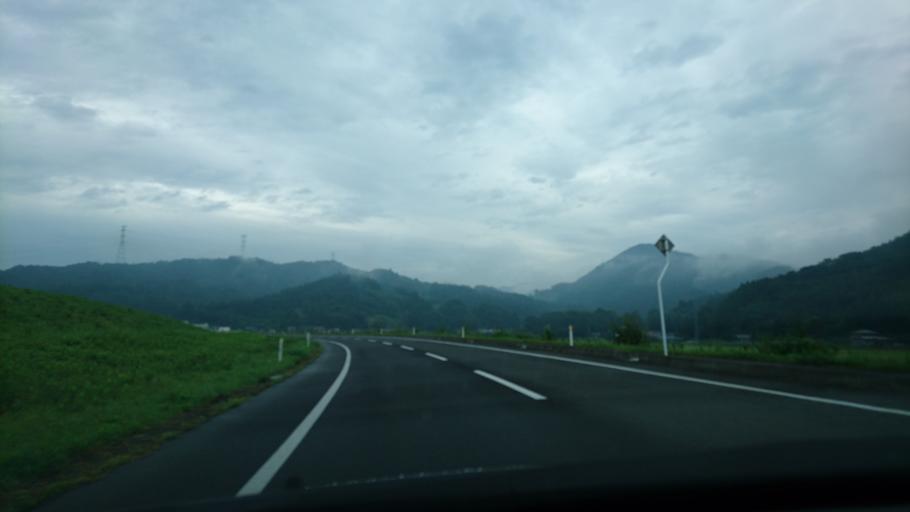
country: JP
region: Iwate
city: Ichinoseki
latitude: 38.9261
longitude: 141.2576
